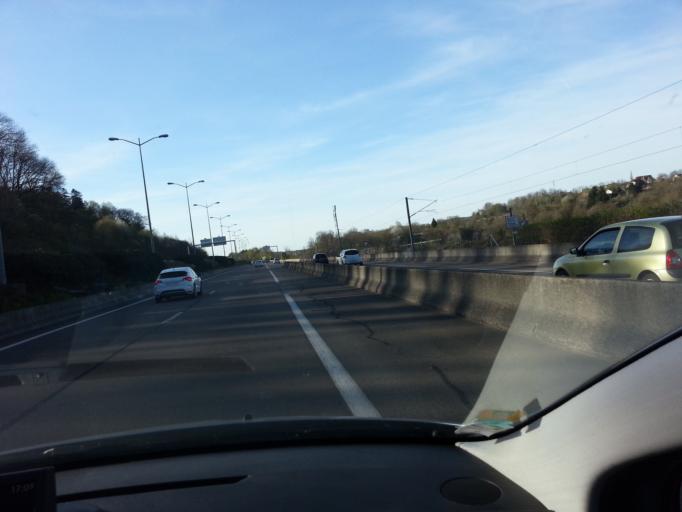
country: FR
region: Franche-Comte
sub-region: Departement du Doubs
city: Besancon
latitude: 47.2660
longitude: 6.0048
